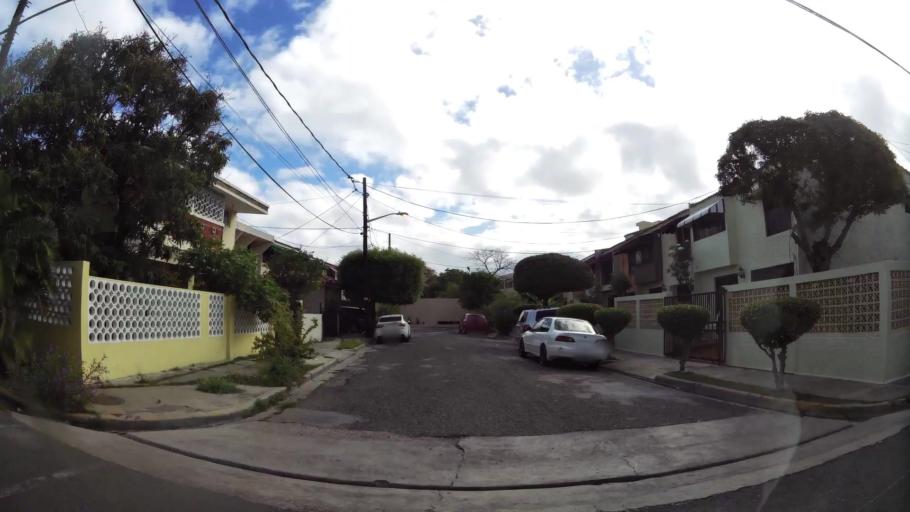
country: DO
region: Nacional
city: Bella Vista
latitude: 18.4439
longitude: -69.9288
